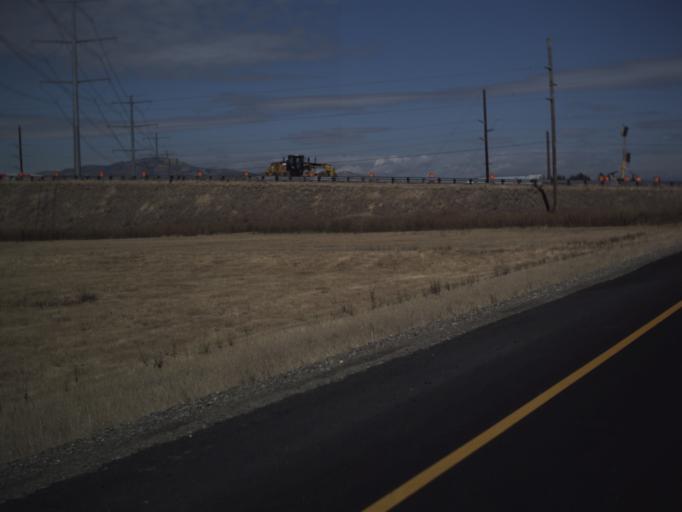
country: US
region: Utah
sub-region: Box Elder County
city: Honeyville
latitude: 41.6337
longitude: -112.0983
